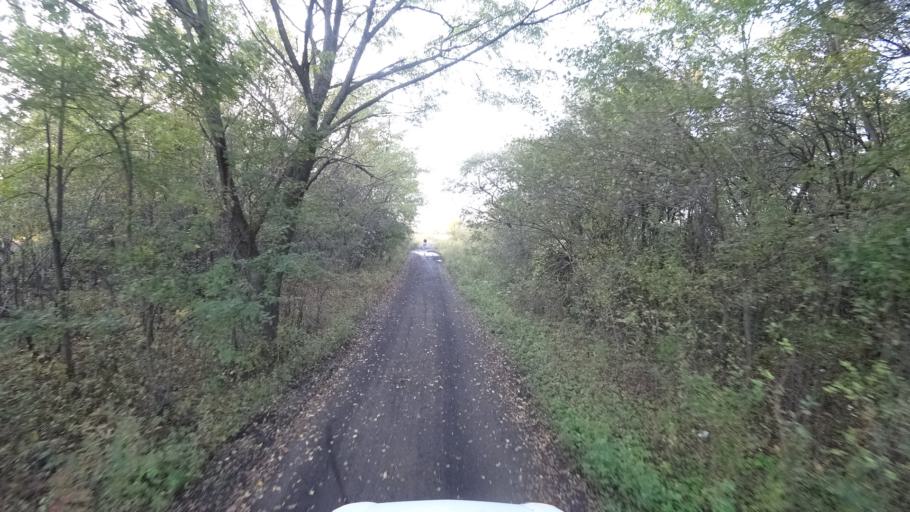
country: RU
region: Amur
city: Arkhara
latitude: 49.3641
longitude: 130.1204
